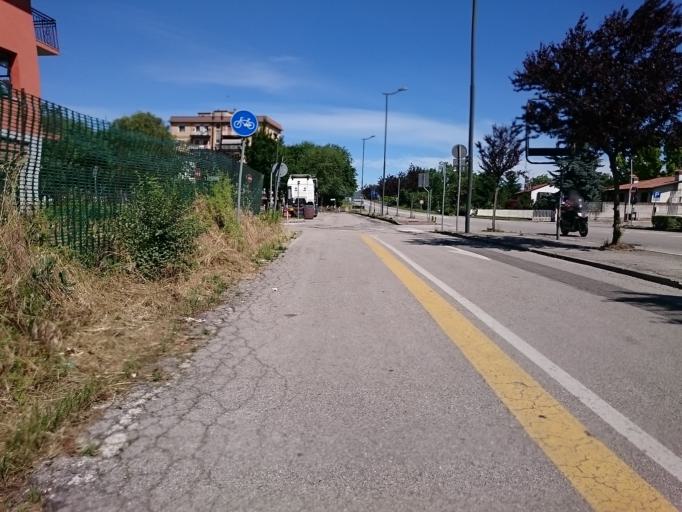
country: IT
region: Veneto
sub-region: Provincia di Padova
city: Piove di Sacco-Piovega
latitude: 45.3003
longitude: 12.0387
